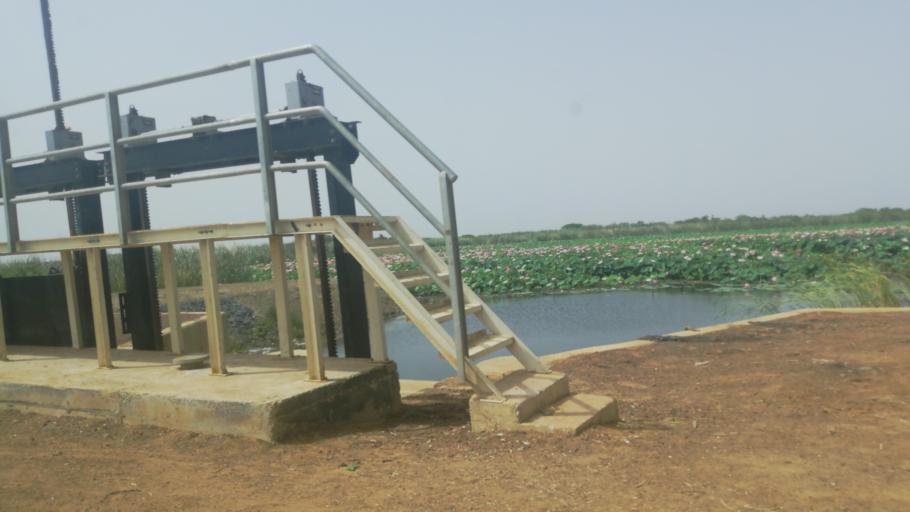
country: SN
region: Saint-Louis
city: Saint-Louis
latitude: 16.0649
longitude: -16.3186
